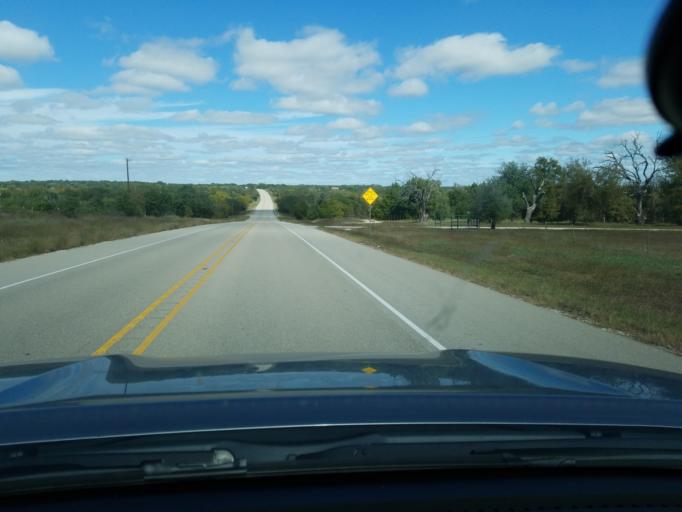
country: US
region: Texas
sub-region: Hamilton County
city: Hamilton
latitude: 31.5790
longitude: -98.1574
